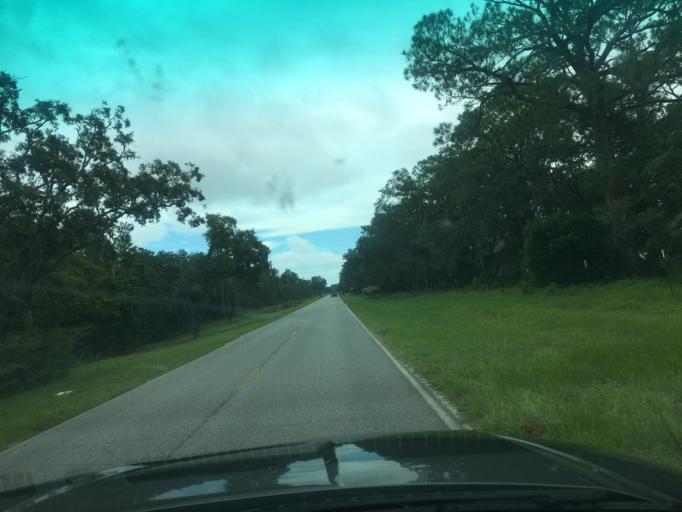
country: US
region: Florida
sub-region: Wakulla County
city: Crawfordville
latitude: 29.9094
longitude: -84.3608
